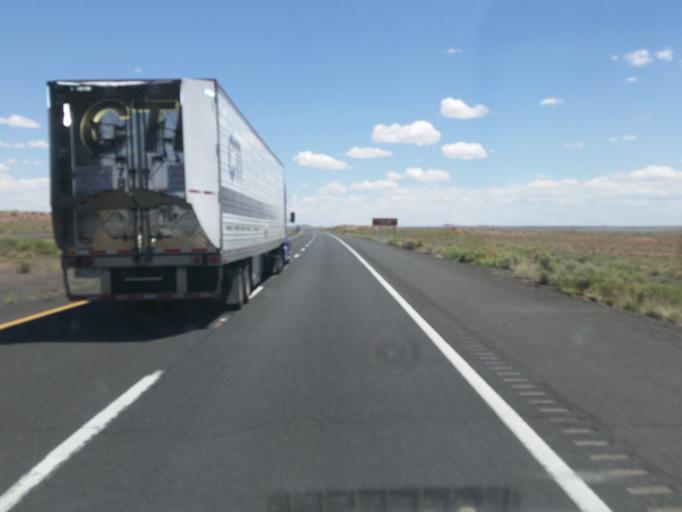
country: US
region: Arizona
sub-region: Navajo County
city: Joseph City
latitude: 34.9159
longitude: -110.2505
